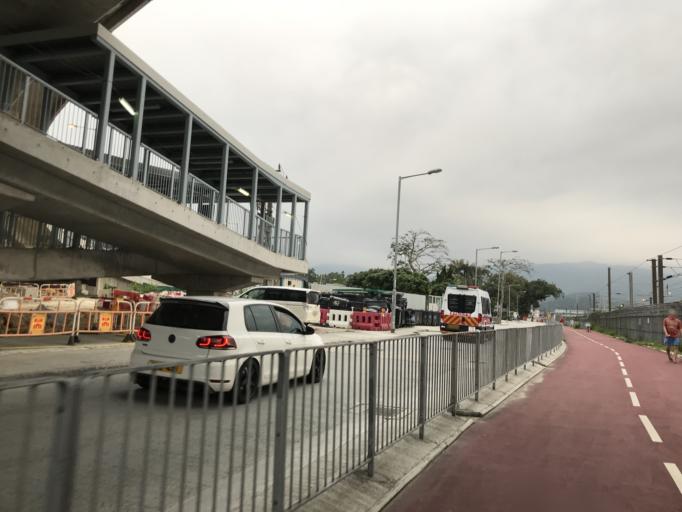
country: HK
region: Tai Po
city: Tai Po
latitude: 22.4750
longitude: 114.1544
